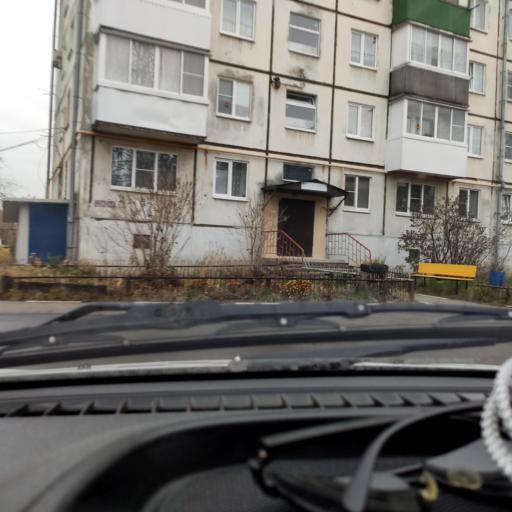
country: RU
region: Samara
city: Zhigulevsk
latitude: 53.4659
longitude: 49.5398
